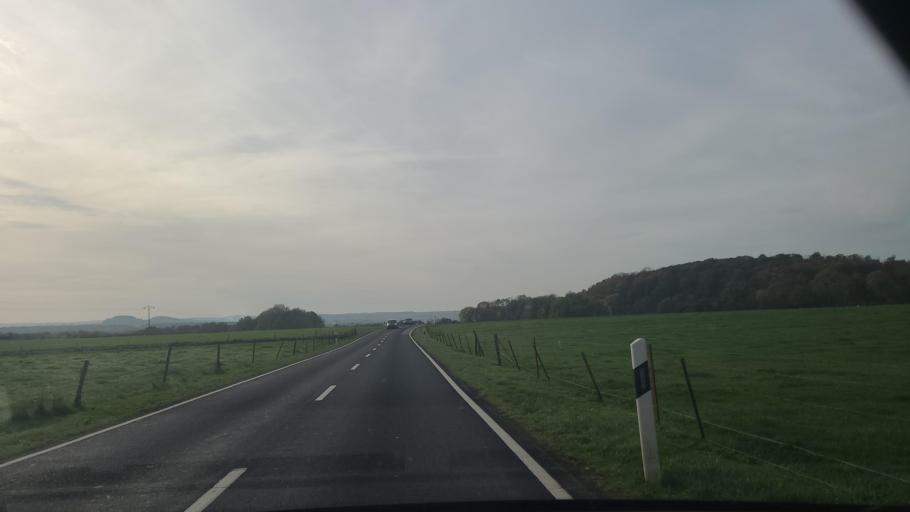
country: LU
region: Luxembourg
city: Hautcharage
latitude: 49.5937
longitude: 5.9135
